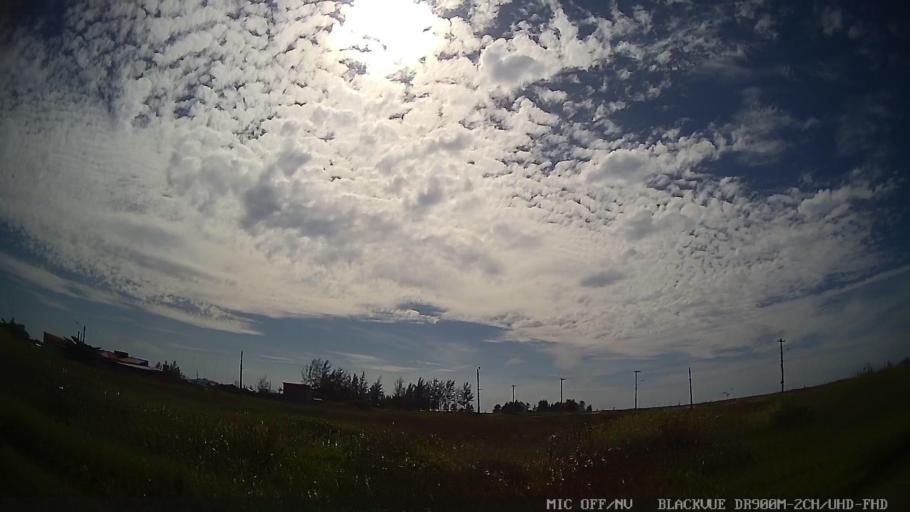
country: BR
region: Sao Paulo
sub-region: Iguape
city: Iguape
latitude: -24.7760
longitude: -47.5956
